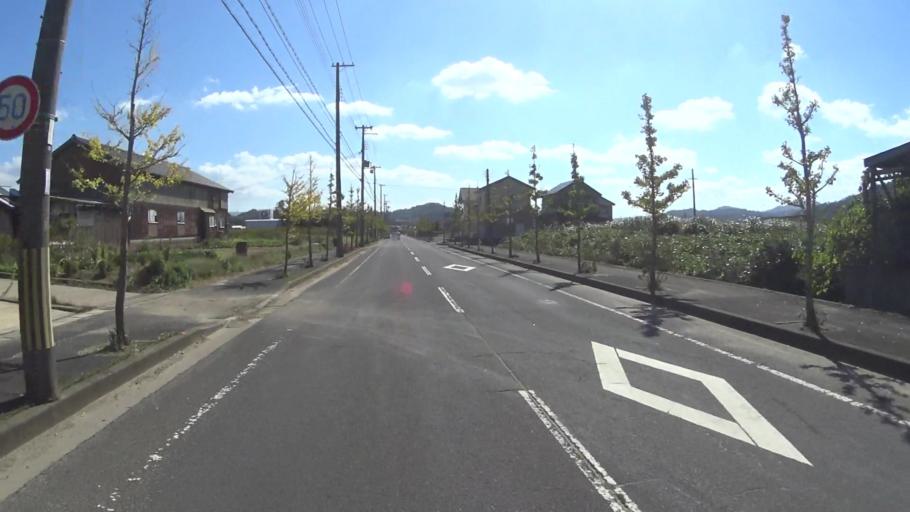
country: JP
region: Kyoto
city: Miyazu
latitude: 35.6816
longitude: 135.0209
